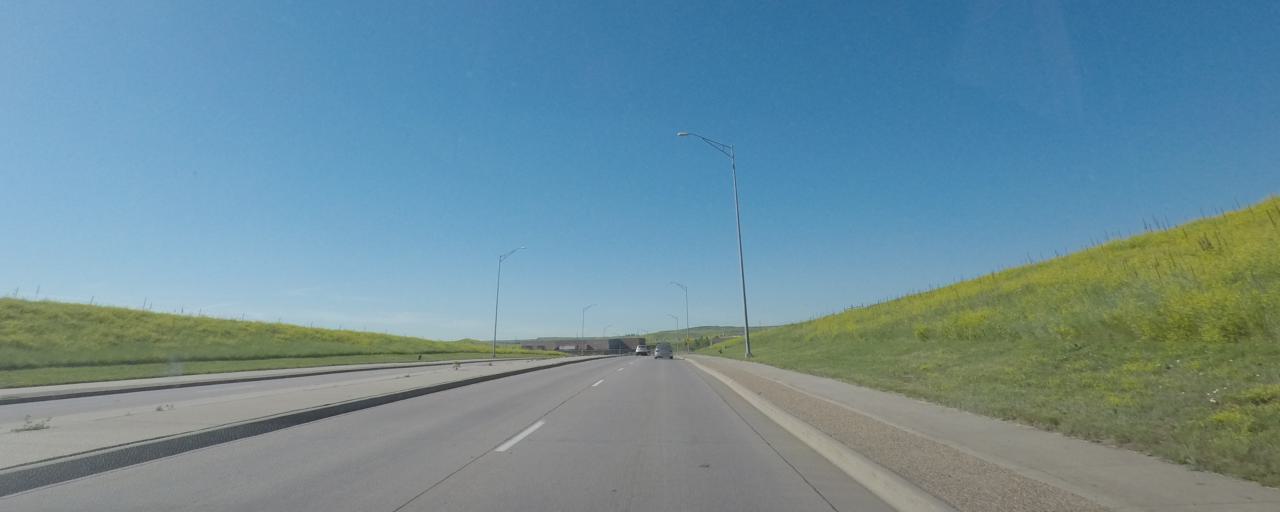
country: US
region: South Dakota
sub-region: Pennington County
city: Rapid City
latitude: 44.0408
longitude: -103.2193
